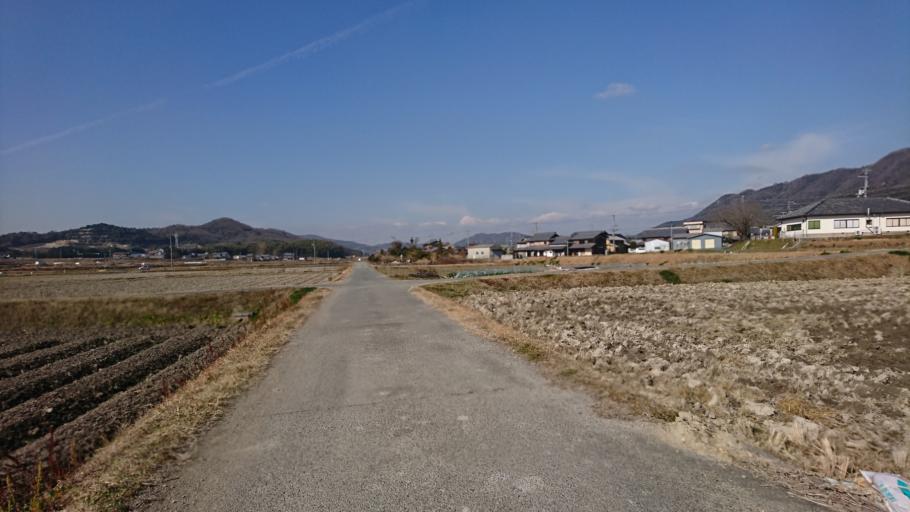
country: JP
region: Hyogo
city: Kakogawacho-honmachi
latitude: 34.8138
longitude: 134.8562
